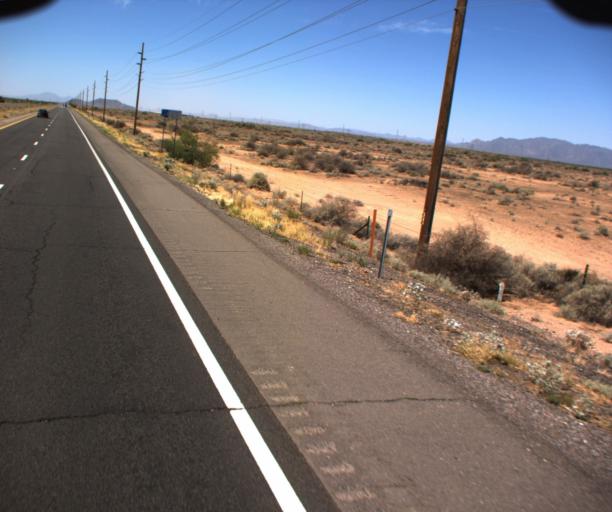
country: US
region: Arizona
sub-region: Maricopa County
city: Sun Lakes
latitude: 33.2463
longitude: -111.9801
